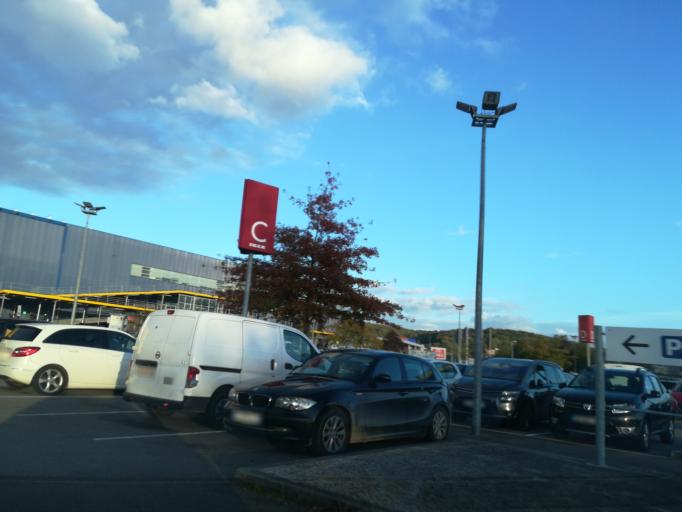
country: FR
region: Haute-Normandie
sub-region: Departement de la Seine-Maritime
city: Oissel
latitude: 49.3315
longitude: 1.0953
